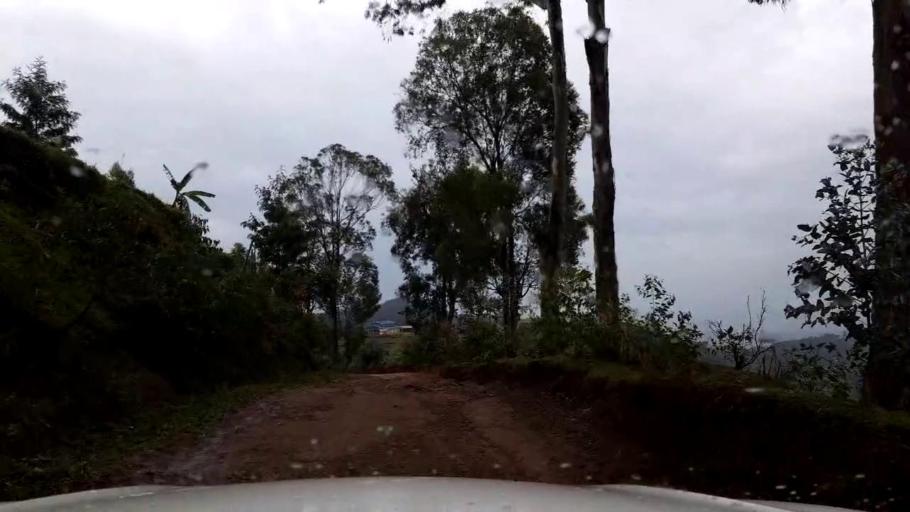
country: RW
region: Western Province
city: Kibuye
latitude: -2.0210
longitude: 29.4616
